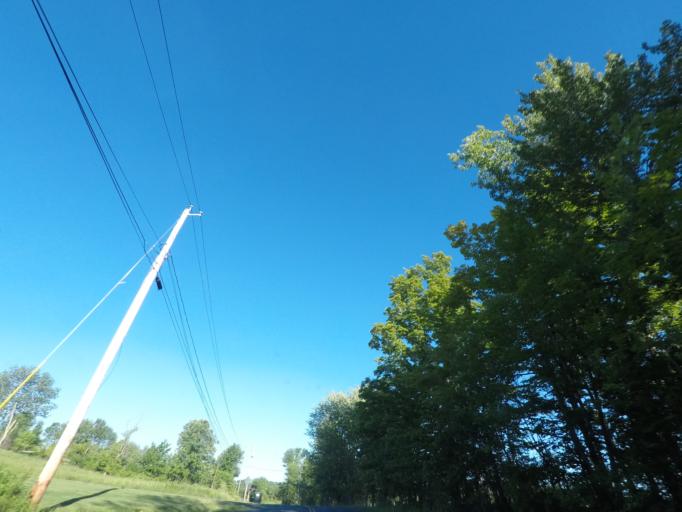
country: US
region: New York
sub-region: Rensselaer County
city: Averill Park
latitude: 42.5810
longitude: -73.5486
